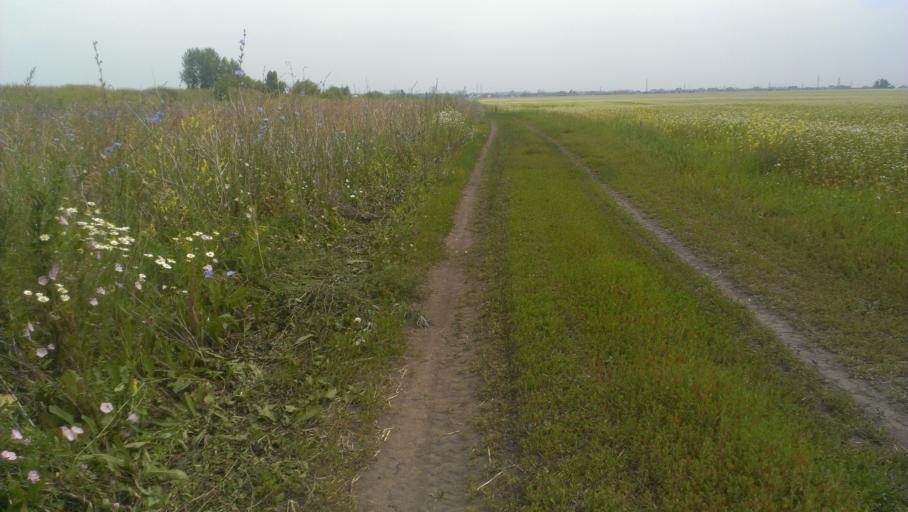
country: RU
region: Altai Krai
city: Gon'ba
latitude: 53.3801
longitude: 83.6320
